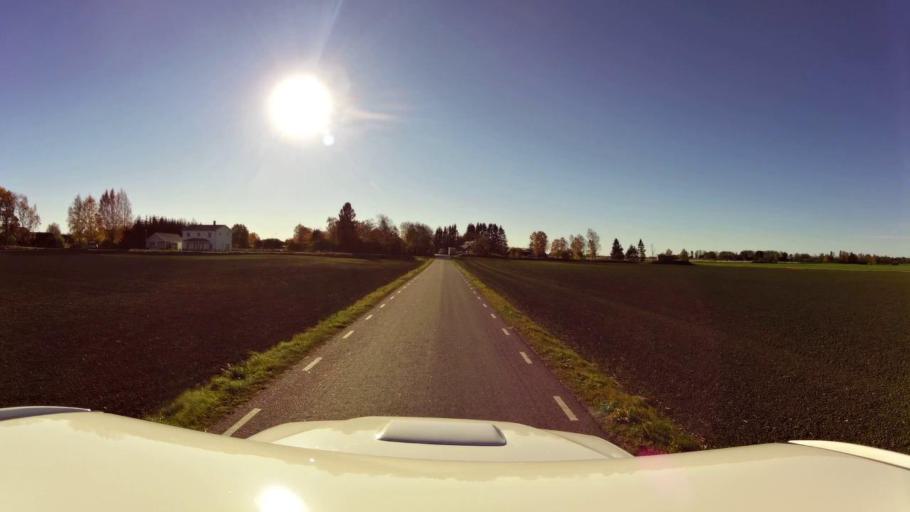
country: SE
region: OEstergoetland
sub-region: Linkopings Kommun
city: Ljungsbro
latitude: 58.4948
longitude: 15.4193
